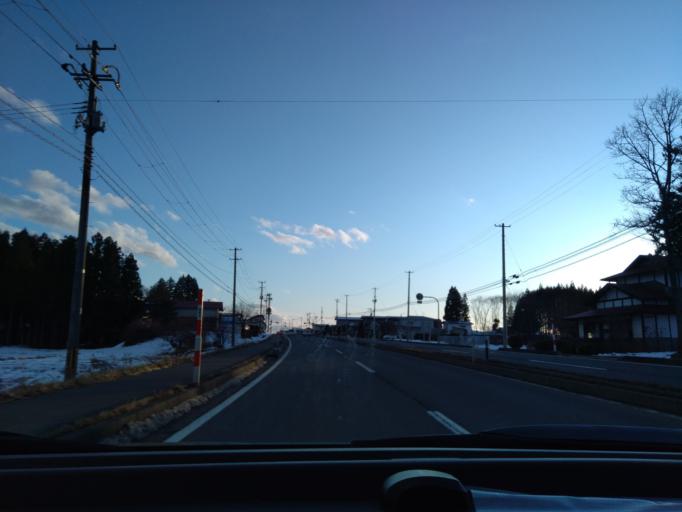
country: JP
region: Iwate
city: Hanamaki
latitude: 39.5290
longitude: 141.1637
